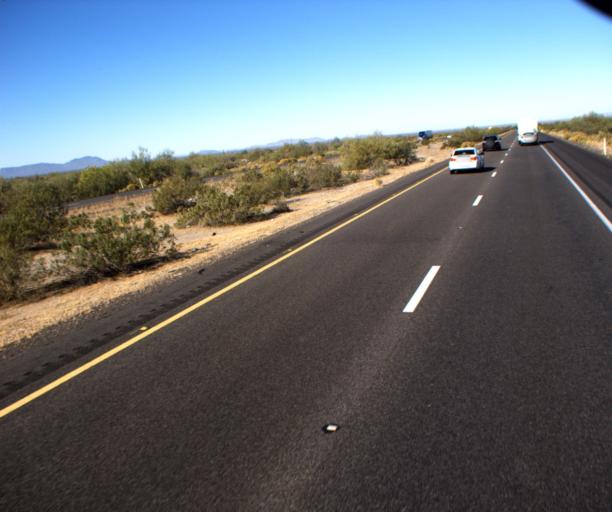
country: US
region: Arizona
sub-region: Maricopa County
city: Gila Bend
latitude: 32.9061
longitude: -112.5703
